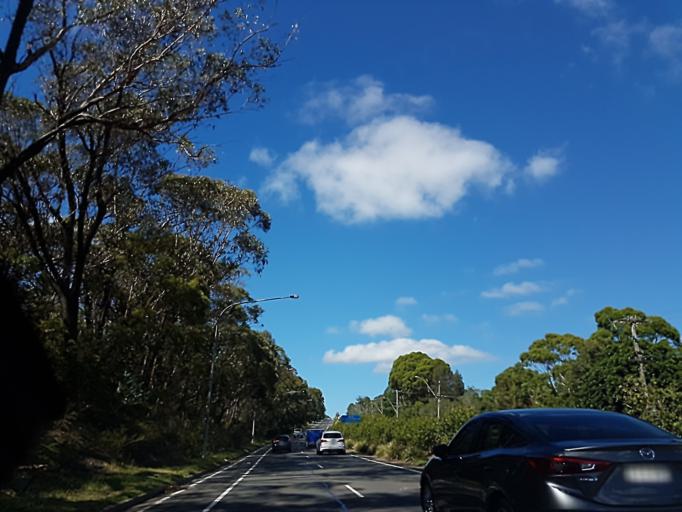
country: AU
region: New South Wales
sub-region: Warringah
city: Davidson
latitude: -33.7127
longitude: 151.2173
